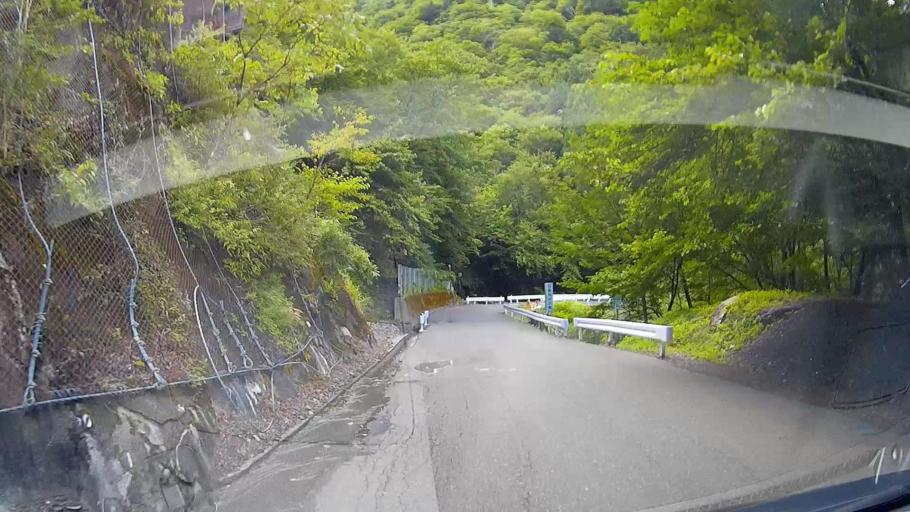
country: JP
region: Shizuoka
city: Shizuoka-shi
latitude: 35.2883
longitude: 138.2167
